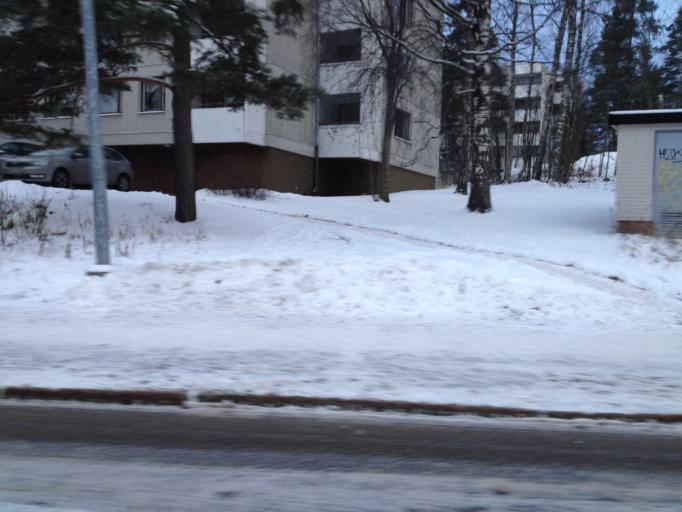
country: FI
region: Uusimaa
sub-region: Helsinki
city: Vantaa
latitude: 60.2160
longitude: 25.1475
